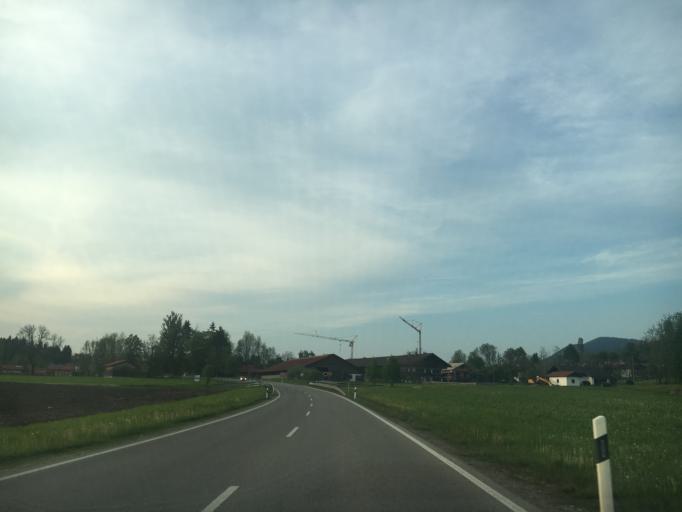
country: DE
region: Bavaria
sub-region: Upper Bavaria
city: Benediktbeuern
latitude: 47.6891
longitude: 11.4058
